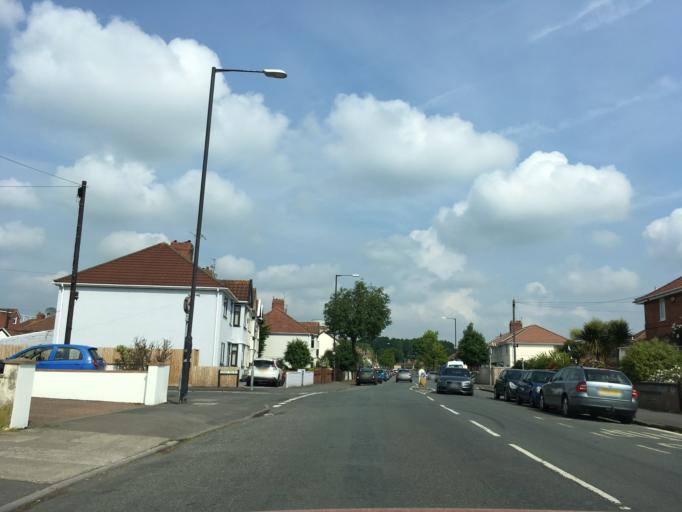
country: GB
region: England
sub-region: Bristol
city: Bristol
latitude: 51.4376
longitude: -2.6143
